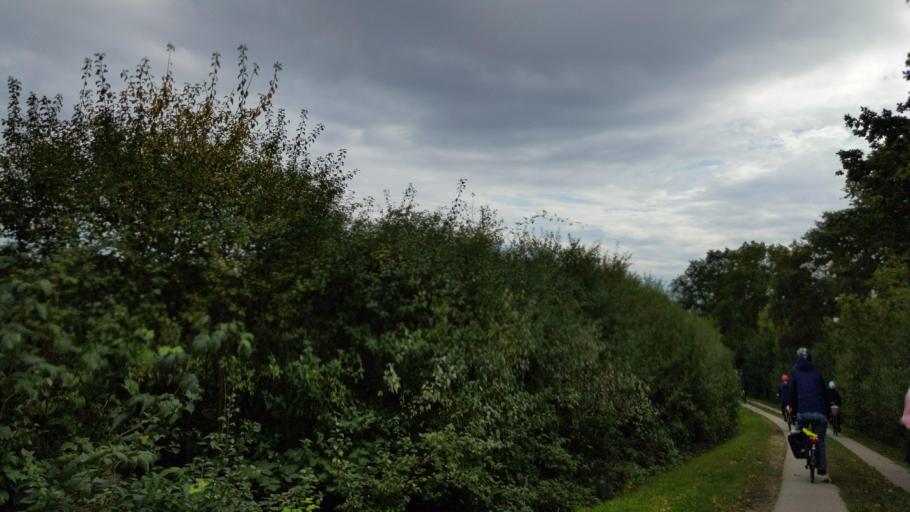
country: DE
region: Mecklenburg-Vorpommern
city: Schlagsdorf
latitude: 53.7321
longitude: 10.8154
